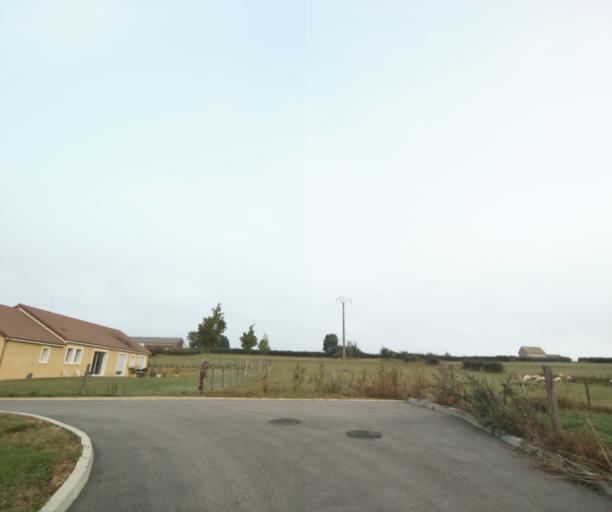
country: FR
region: Bourgogne
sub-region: Departement de Saone-et-Loire
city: Charolles
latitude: 46.4361
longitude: 4.2853
